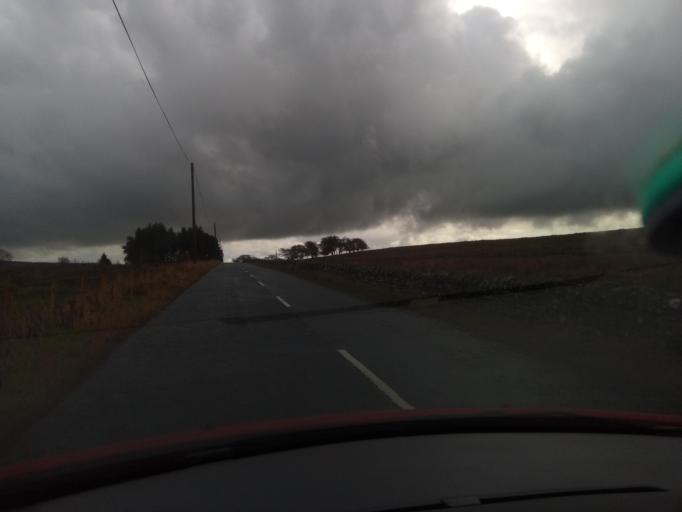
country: GB
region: England
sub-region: Northumberland
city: Birtley
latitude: 55.1276
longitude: -2.2372
